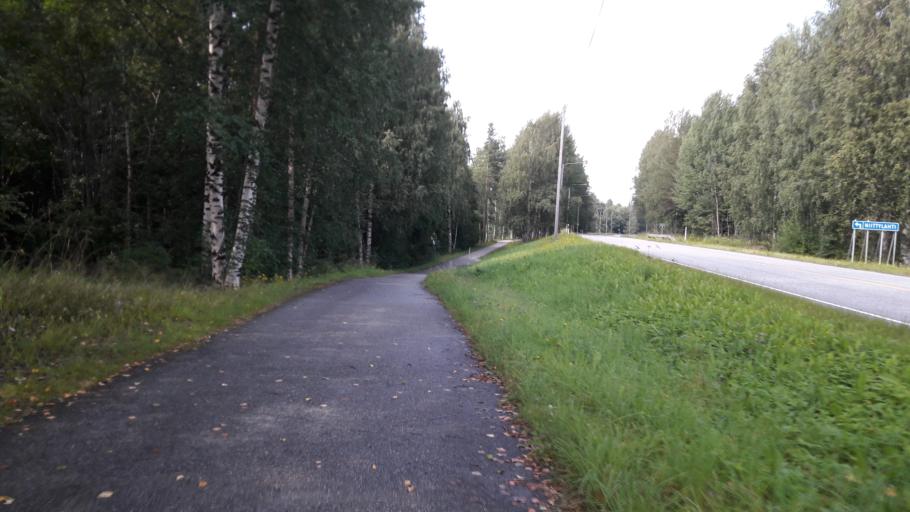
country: FI
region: North Karelia
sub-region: Joensuu
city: Pyhaeselkae
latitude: 62.5195
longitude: 29.8674
